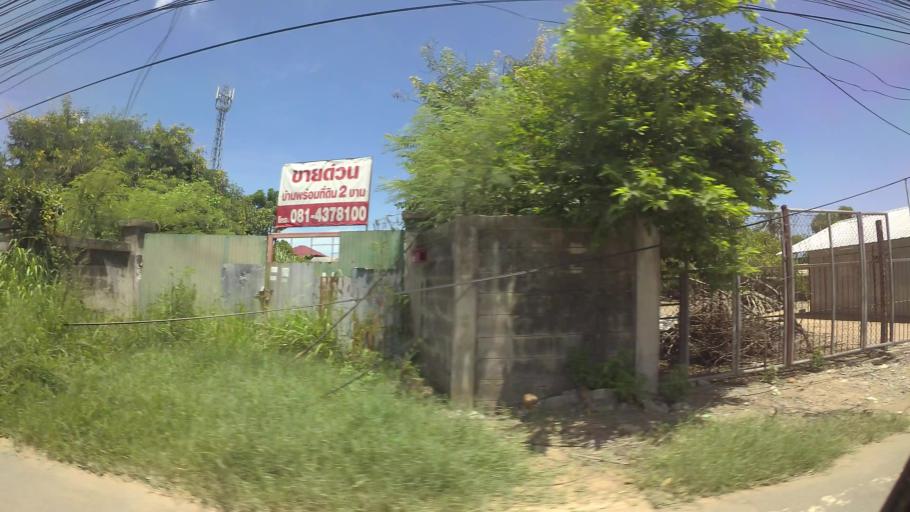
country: TH
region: Chon Buri
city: Si Racha
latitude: 13.1257
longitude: 100.9539
